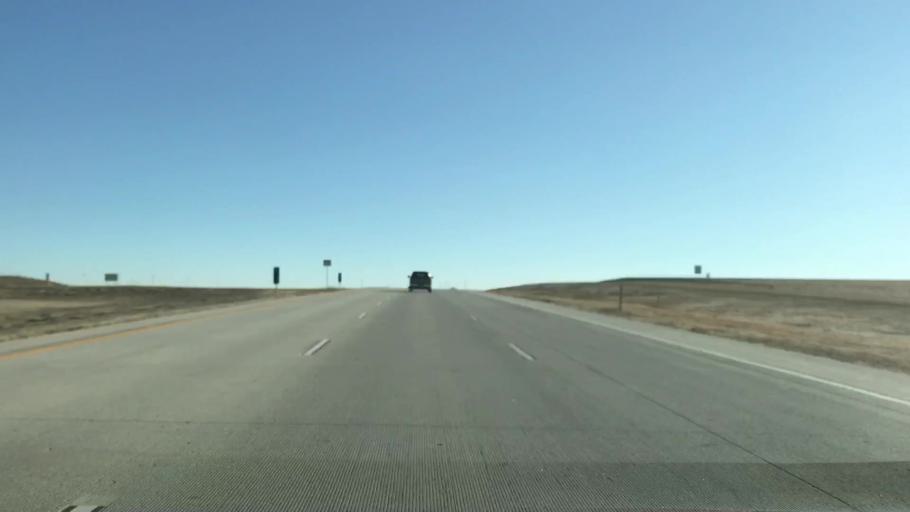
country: US
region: Colorado
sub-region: Lincoln County
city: Limon
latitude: 39.2641
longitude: -103.6383
